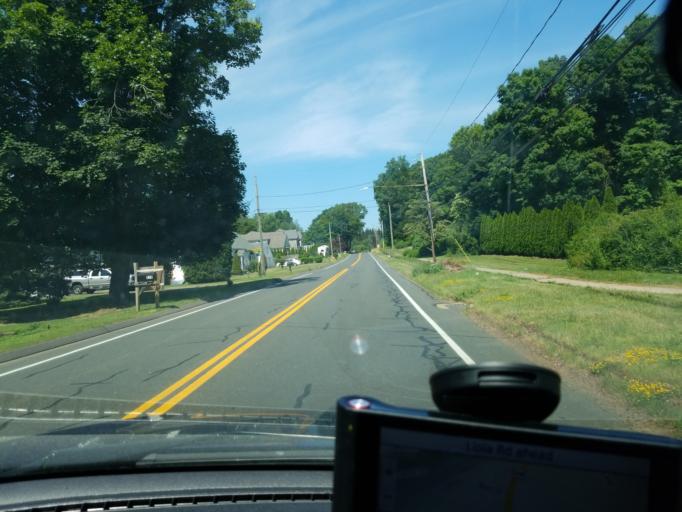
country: US
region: Connecticut
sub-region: Hartford County
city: Newington
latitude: 41.6493
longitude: -72.7108
